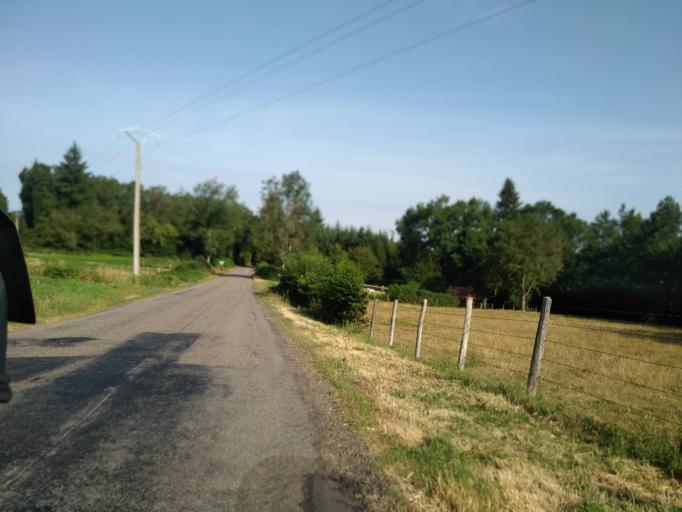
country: FR
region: Rhone-Alpes
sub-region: Departement de la Loire
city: Saint-Nizier-sous-Charlieu
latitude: 46.2400
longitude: 4.1266
